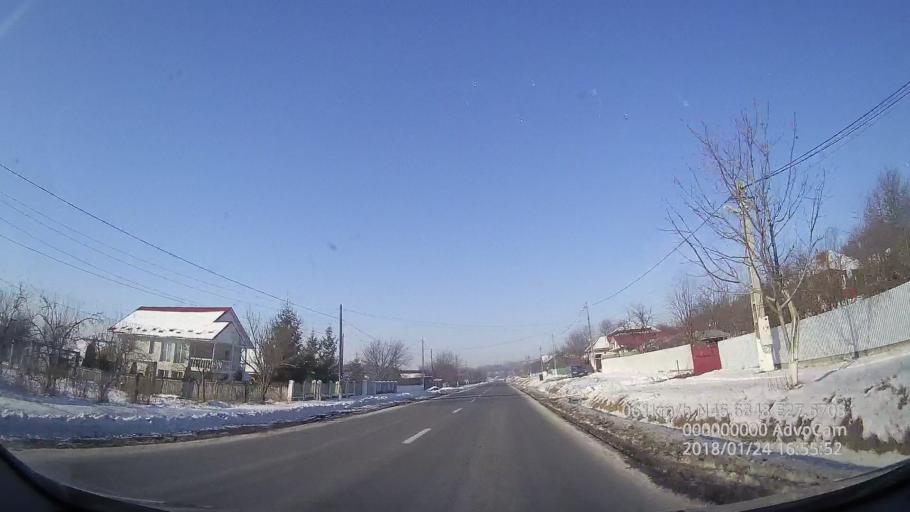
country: RO
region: Vaslui
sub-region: Municipiul Vaslui
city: Brodoc
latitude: 46.6852
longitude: 27.6706
